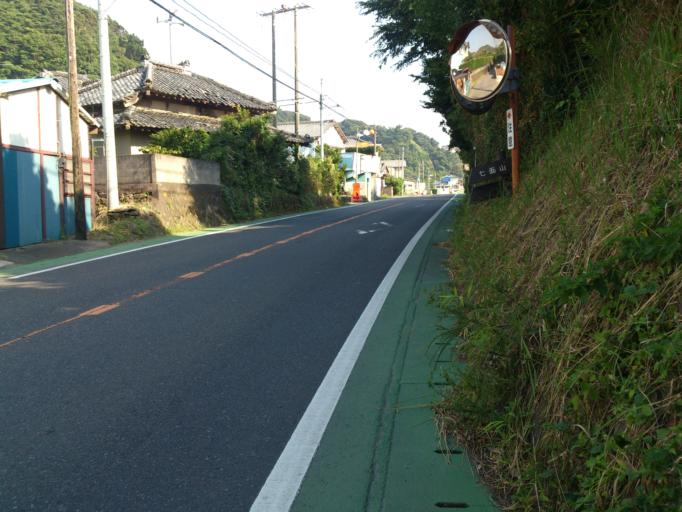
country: JP
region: Chiba
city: Tateyama
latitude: 35.0586
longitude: 139.8283
